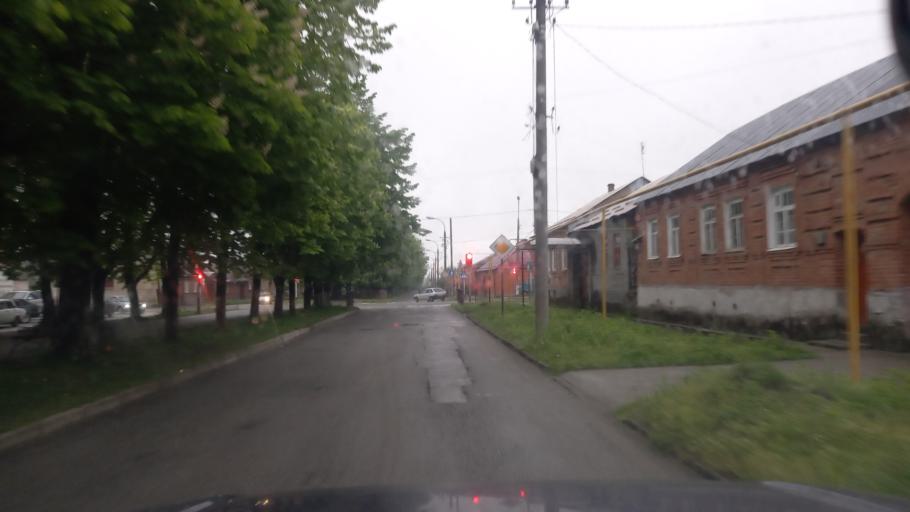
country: RU
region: North Ossetia
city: Alagir
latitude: 43.0418
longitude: 44.2203
